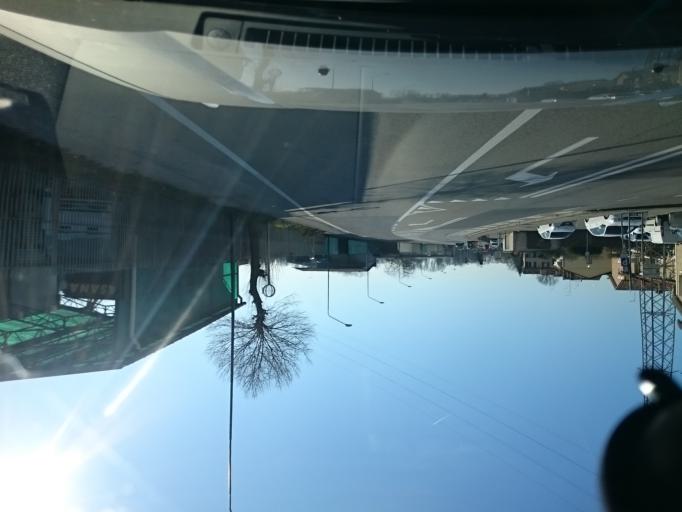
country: IT
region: Veneto
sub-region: Provincia di Venezia
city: Mestre
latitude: 45.4810
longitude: 12.2569
